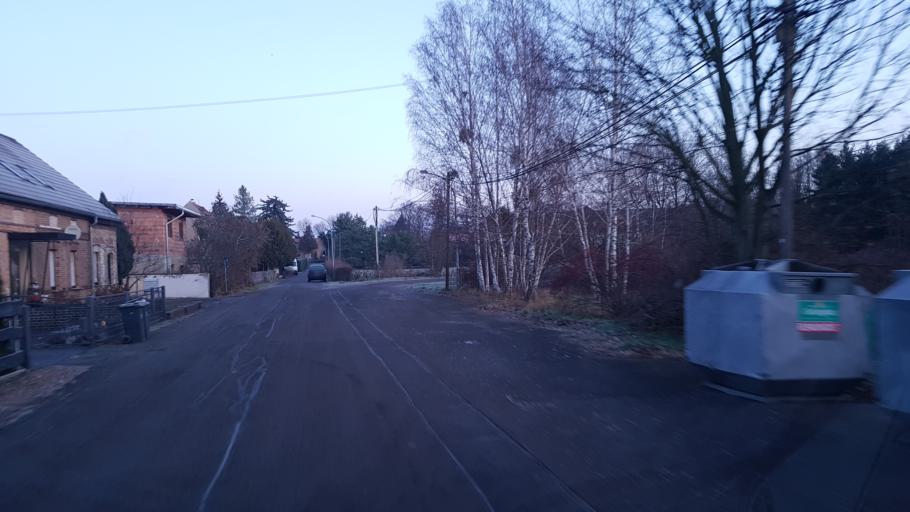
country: DE
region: Brandenburg
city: Schipkau
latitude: 51.5520
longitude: 13.8860
